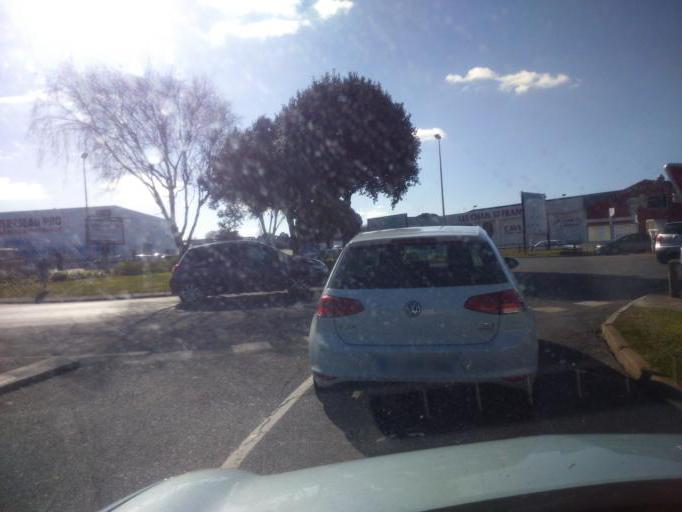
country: FR
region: Pays de la Loire
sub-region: Departement de la Loire-Atlantique
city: Guerande
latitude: 47.3275
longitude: -2.4129
